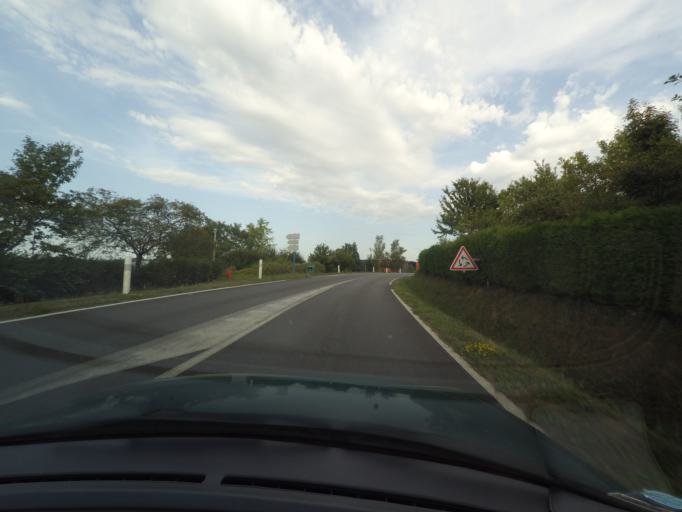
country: FR
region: Limousin
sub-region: Departement de la Haute-Vienne
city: Saint-Priest-sous-Aixe
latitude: 45.8011
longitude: 1.1155
